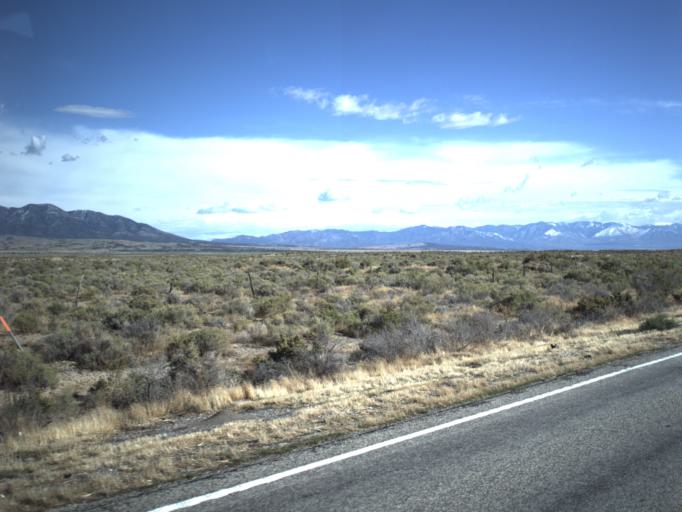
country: US
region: Utah
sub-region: Millard County
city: Delta
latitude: 39.3114
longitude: -112.4773
